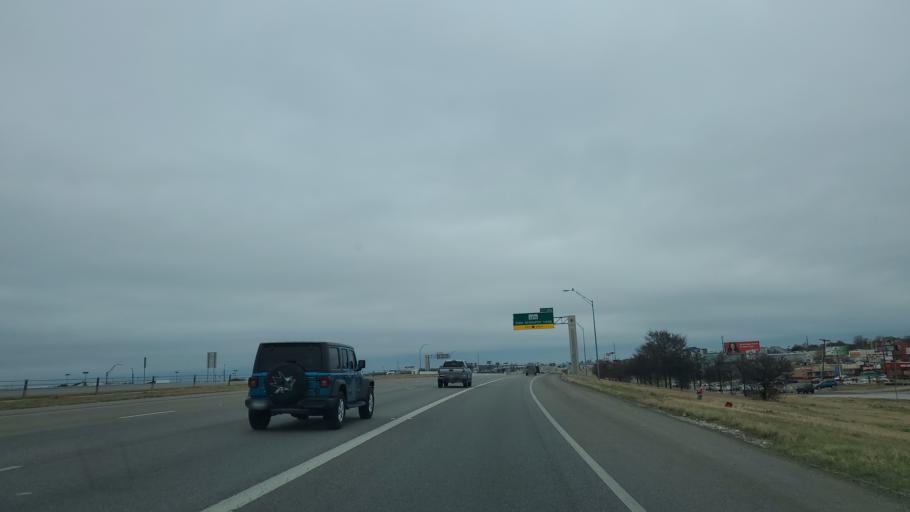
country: US
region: Texas
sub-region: Bell County
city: Killeen
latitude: 31.0918
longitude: -97.7221
